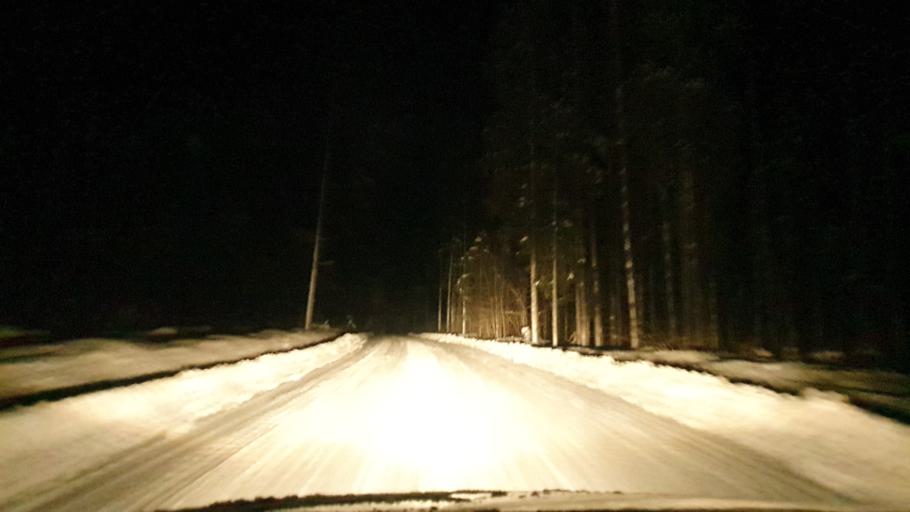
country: EE
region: Vorumaa
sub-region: Antsla vald
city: Vana-Antsla
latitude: 57.9463
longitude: 26.6087
